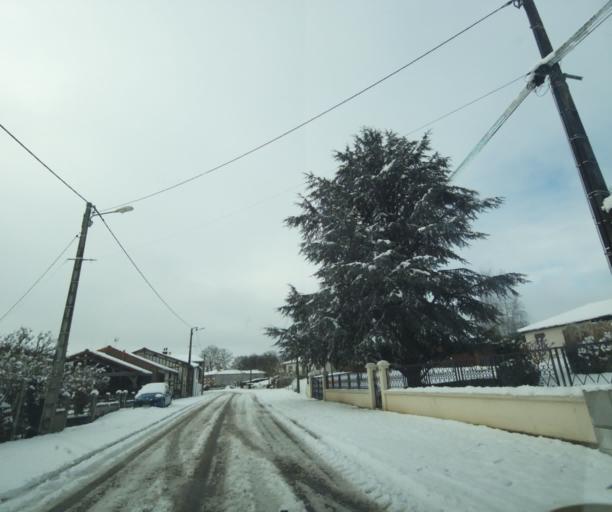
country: FR
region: Champagne-Ardenne
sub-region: Departement de la Haute-Marne
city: Montier-en-Der
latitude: 48.5147
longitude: 4.6981
